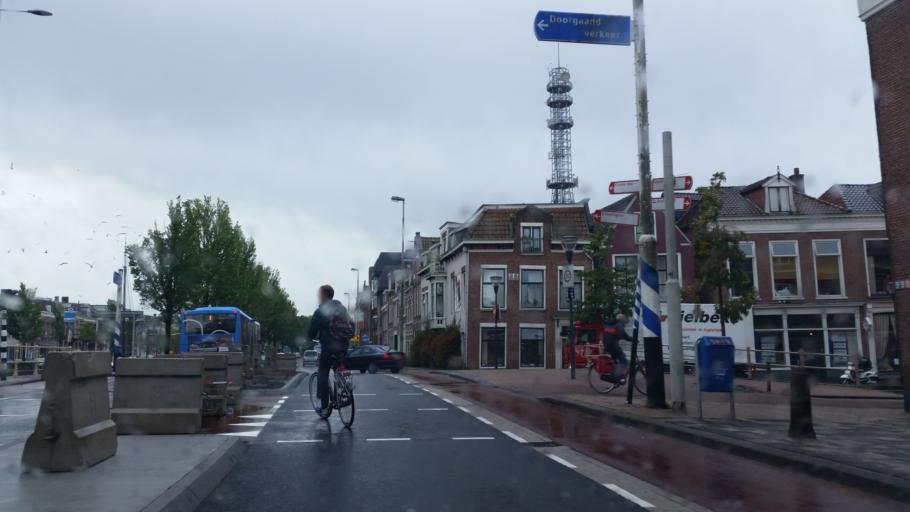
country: NL
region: Friesland
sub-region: Gemeente Leeuwarden
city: Leeuwarden
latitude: 53.2031
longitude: 5.8031
